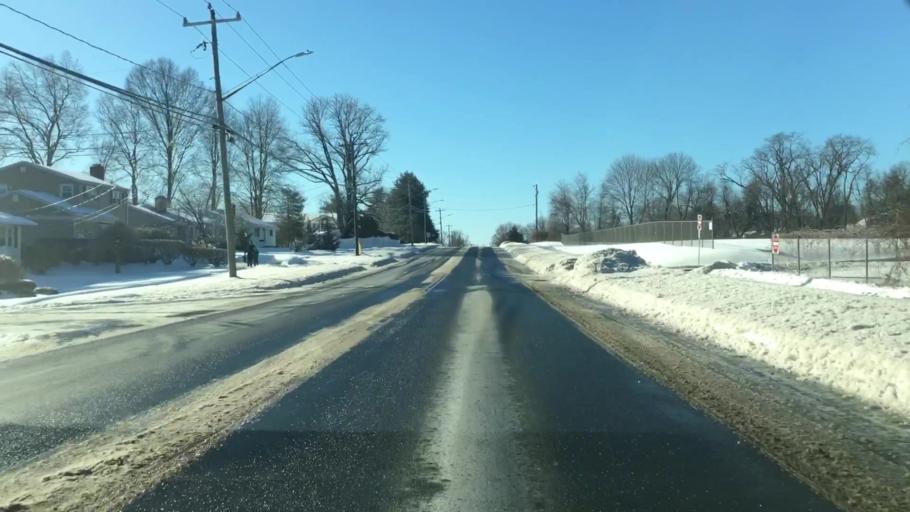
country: US
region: Connecticut
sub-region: Hartford County
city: Newington
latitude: 41.7144
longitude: -72.7436
